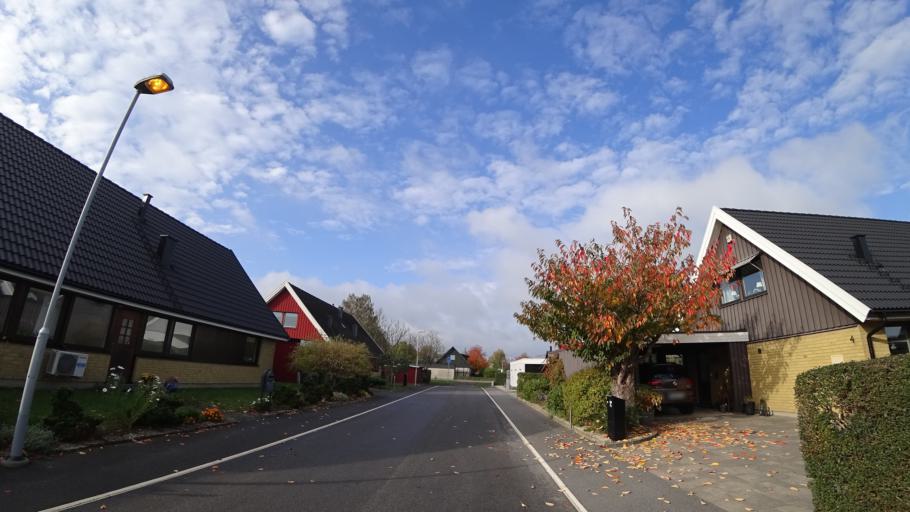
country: SE
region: Skane
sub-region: Staffanstorps Kommun
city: Staffanstorp
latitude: 55.6410
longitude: 13.1910
